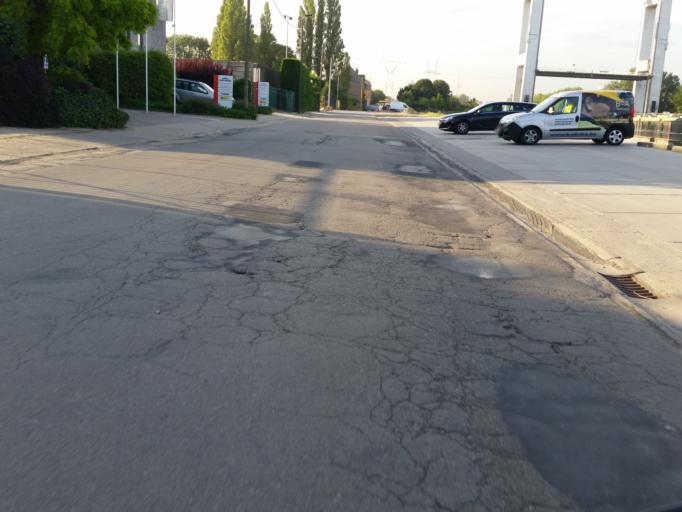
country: BE
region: Flanders
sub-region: Provincie Vlaams-Brabant
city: Vilvoorde
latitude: 50.9504
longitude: 4.4127
